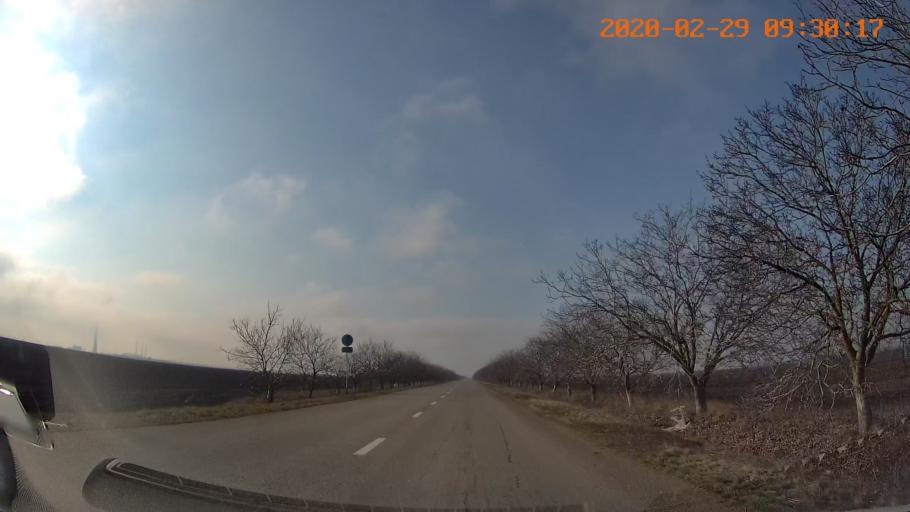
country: UA
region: Odessa
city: Lymanske
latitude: 46.6683
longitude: 29.9173
